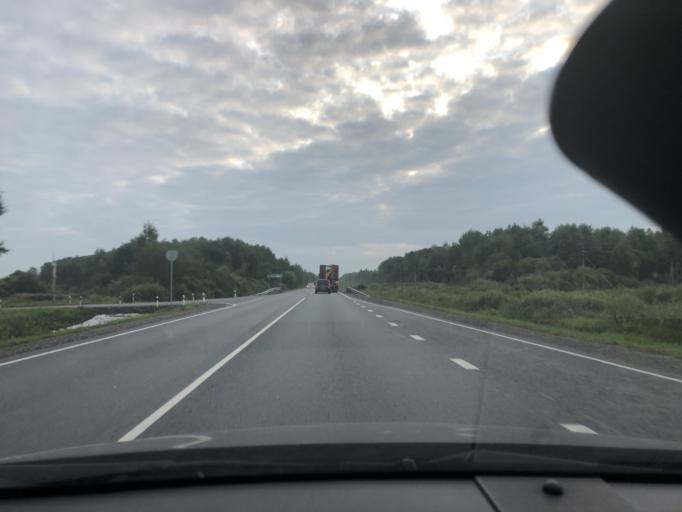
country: RU
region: Kaluga
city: Ferzikovo
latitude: 54.3579
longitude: 36.7718
